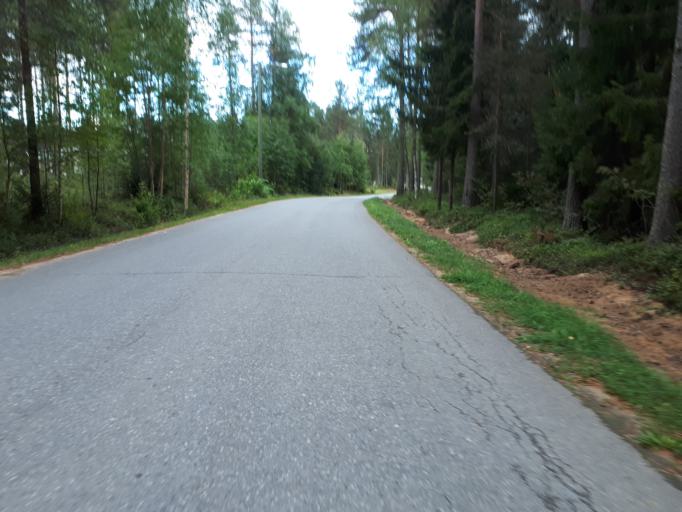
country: FI
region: Northern Ostrobothnia
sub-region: Oulunkaari
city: Ii
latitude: 65.3271
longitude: 25.3919
